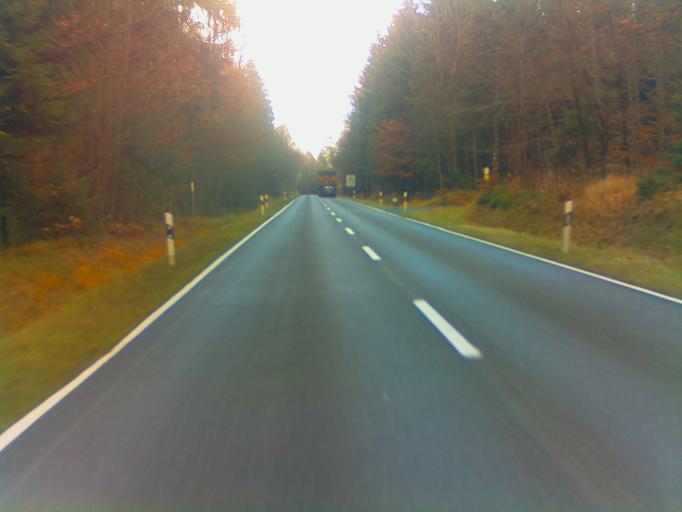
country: DE
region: Thuringia
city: Hildburghausen
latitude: 50.4535
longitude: 10.7408
